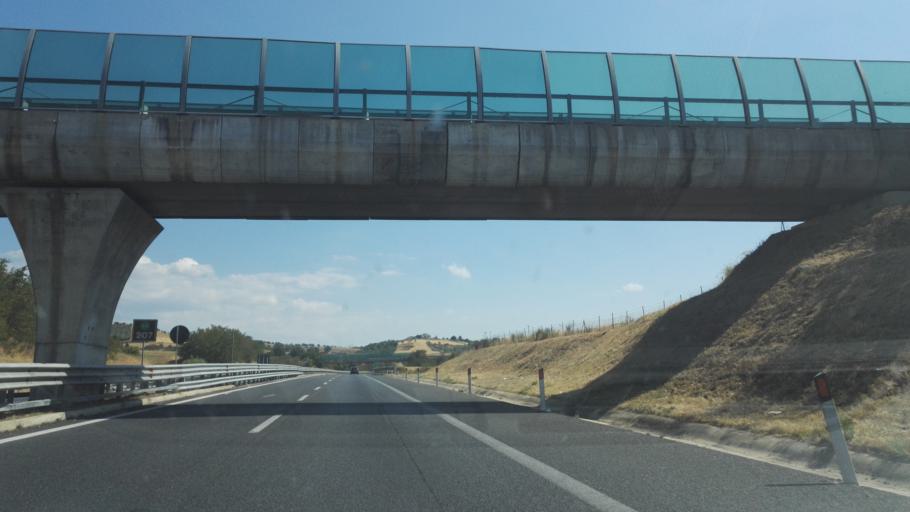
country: IT
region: Calabria
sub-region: Provincia di Cosenza
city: Tarsia
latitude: 39.6221
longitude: 16.2292
